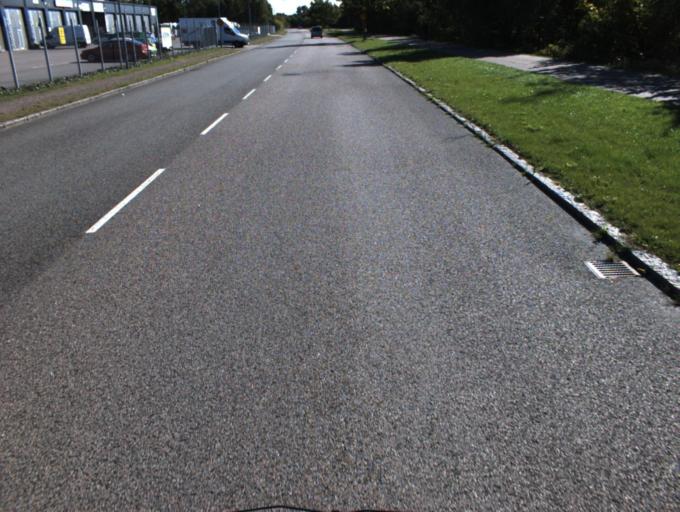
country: SE
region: Skane
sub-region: Helsingborg
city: Helsingborg
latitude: 56.0124
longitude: 12.7187
